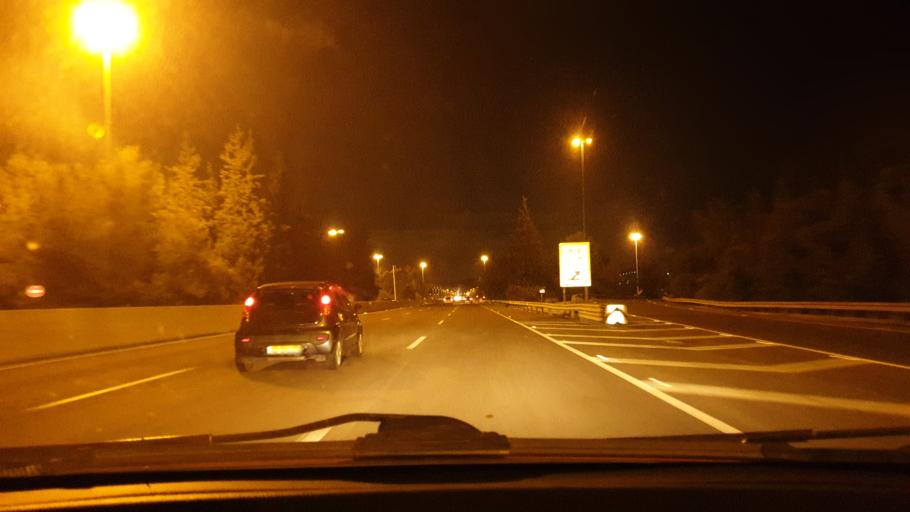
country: IL
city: Nof Ayalon
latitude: 31.8365
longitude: 34.9877
